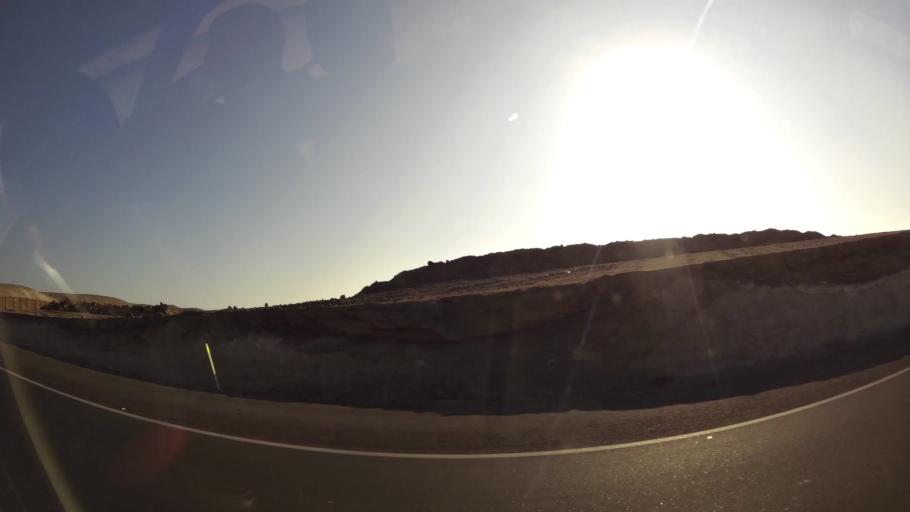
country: PE
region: Ica
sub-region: Provincia de Pisco
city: San Clemente
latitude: -13.6355
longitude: -76.1731
